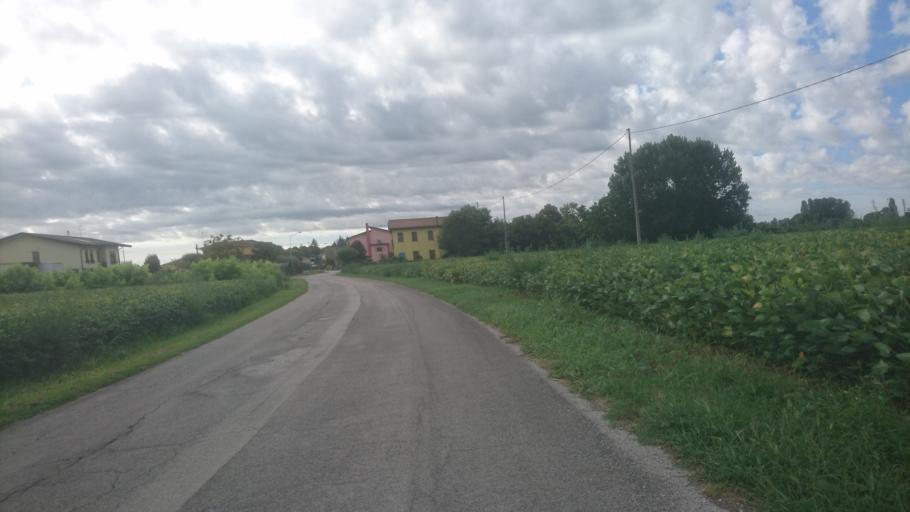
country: IT
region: Veneto
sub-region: Provincia di Venezia
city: Vigonovo
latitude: 45.3974
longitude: 11.9980
